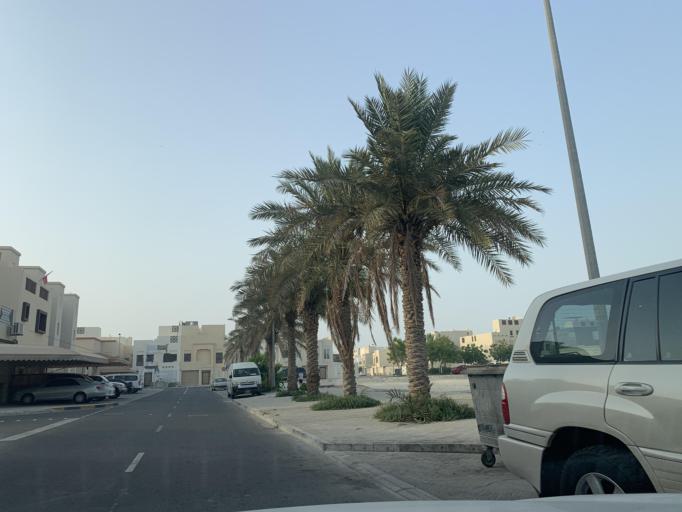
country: BH
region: Manama
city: Jidd Hafs
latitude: 26.2197
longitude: 50.4406
